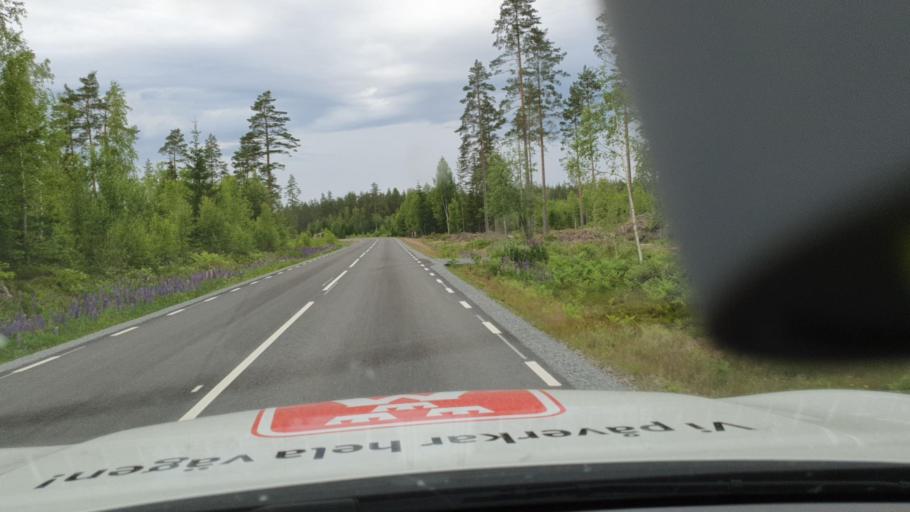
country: SE
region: OErebro
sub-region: Laxa Kommun
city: Laxa
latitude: 58.8684
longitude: 14.5318
